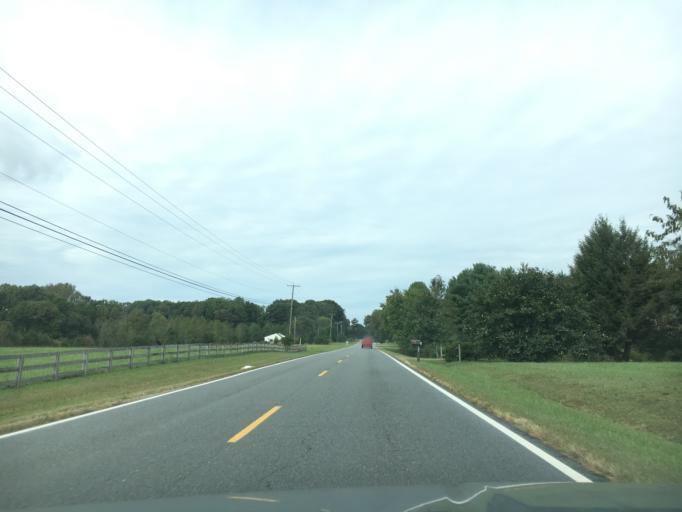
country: US
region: Virginia
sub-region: Goochland County
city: Goochland
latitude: 37.7280
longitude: -77.8336
